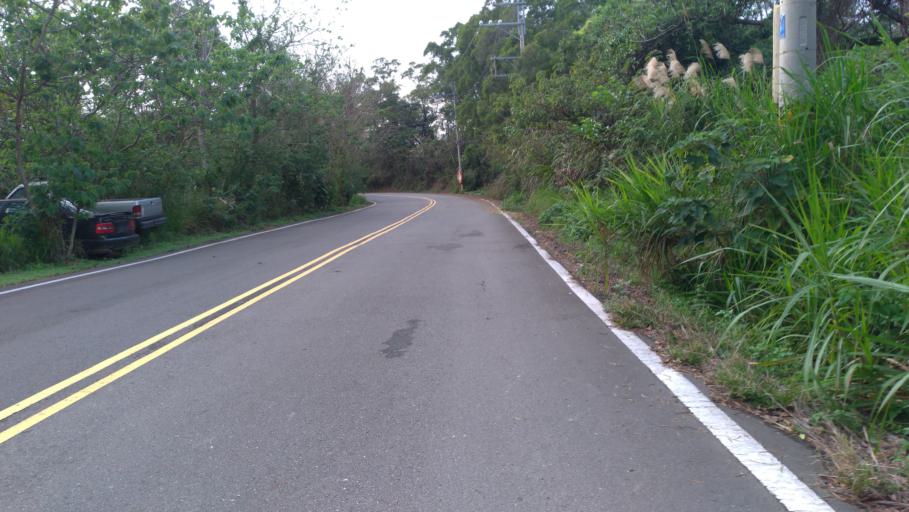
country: TW
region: Taiwan
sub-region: Hsinchu
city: Hsinchu
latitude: 24.7539
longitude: 120.9906
